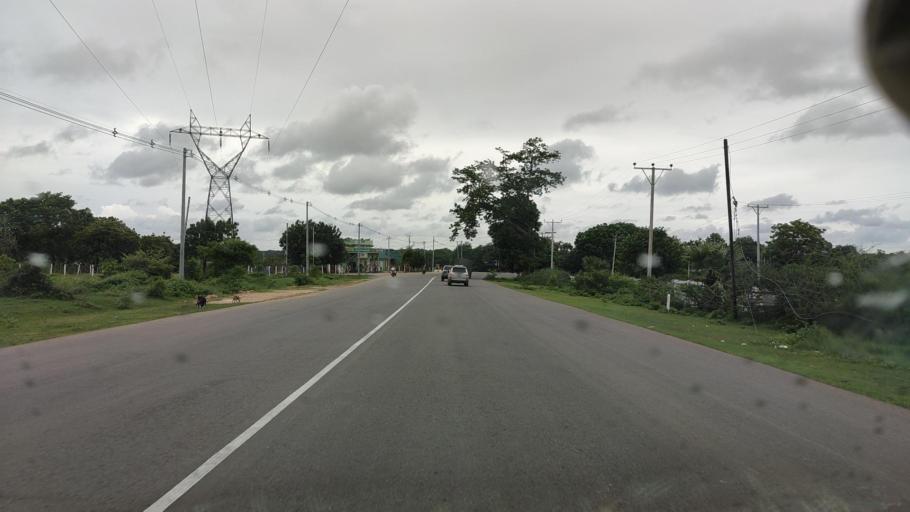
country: MM
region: Mandalay
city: Meiktila
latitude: 20.8345
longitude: 95.8970
